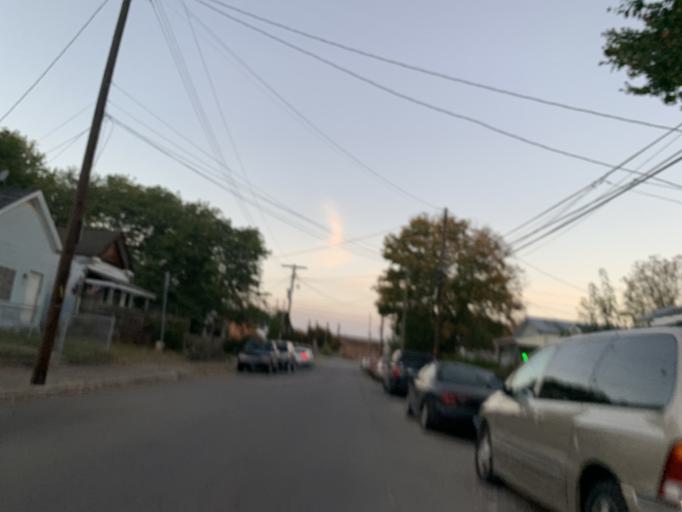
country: US
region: Kentucky
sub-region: Jefferson County
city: Louisville
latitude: 38.2286
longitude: -85.7699
